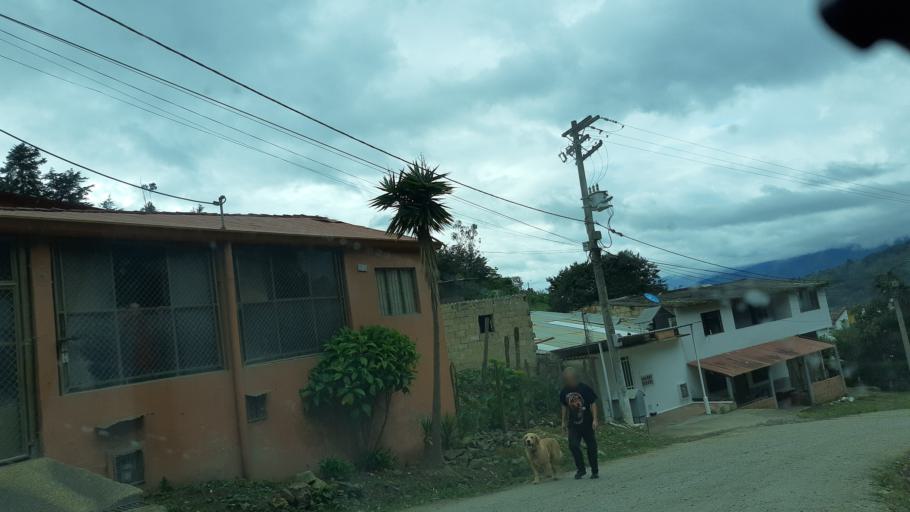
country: CO
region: Boyaca
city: Garagoa
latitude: 5.0731
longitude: -73.3634
